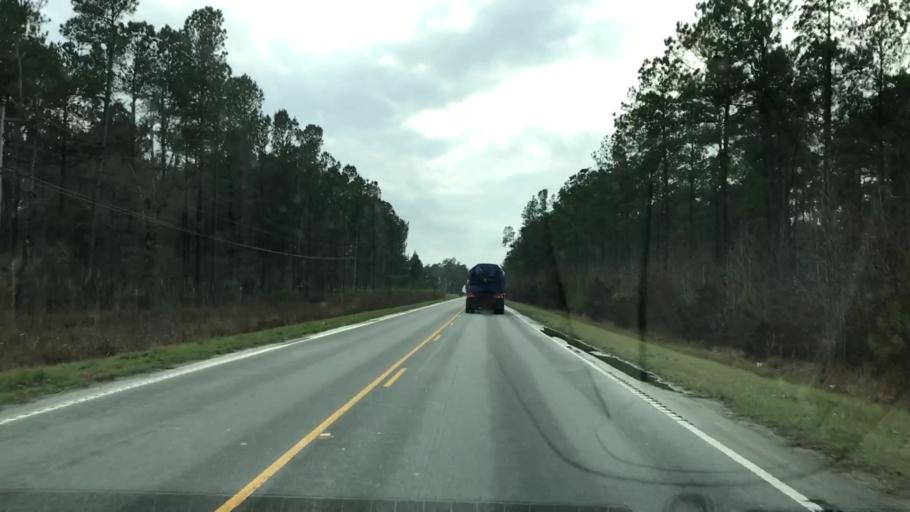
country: US
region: South Carolina
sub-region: Berkeley County
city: Bonneau Beach
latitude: 33.2630
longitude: -79.9245
